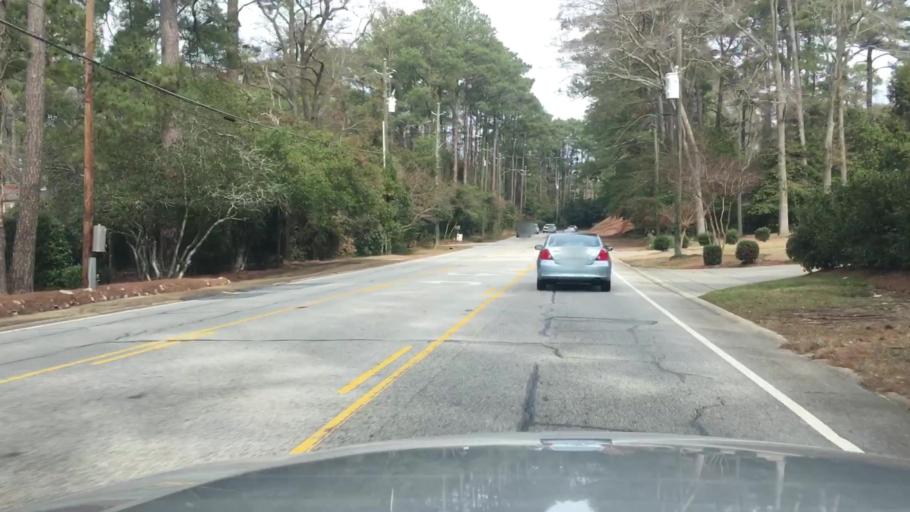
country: US
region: North Carolina
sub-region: Cumberland County
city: Fayetteville
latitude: 35.0515
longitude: -78.9133
